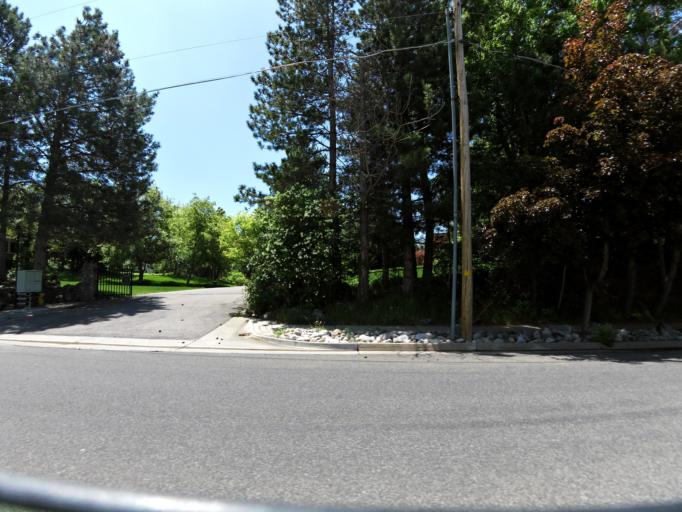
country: US
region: Utah
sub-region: Weber County
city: South Ogden
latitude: 41.1788
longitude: -111.9378
